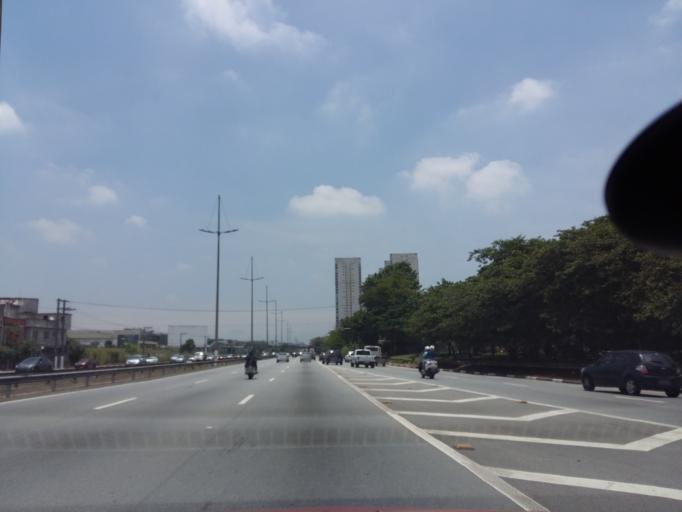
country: BR
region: Sao Paulo
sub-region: Diadema
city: Diadema
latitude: -23.6323
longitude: -46.6302
